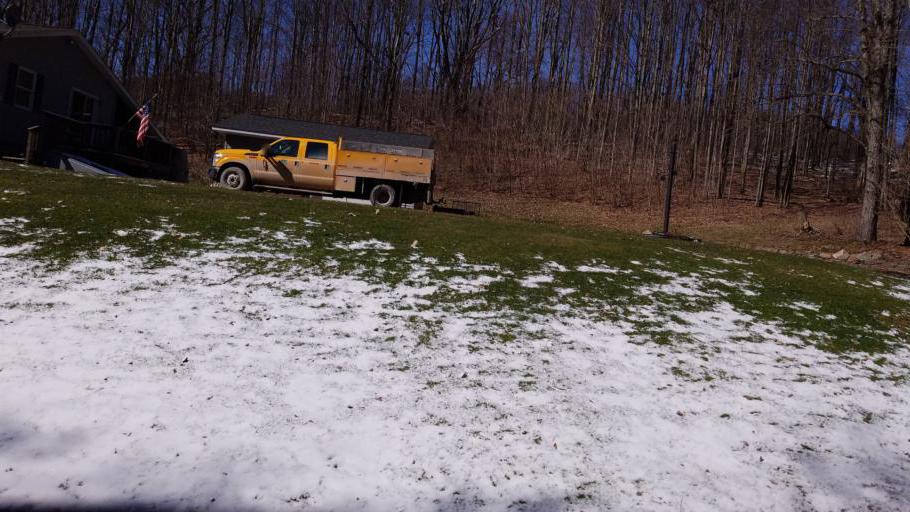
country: US
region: Pennsylvania
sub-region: Tioga County
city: Westfield
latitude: 41.9445
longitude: -77.7300
